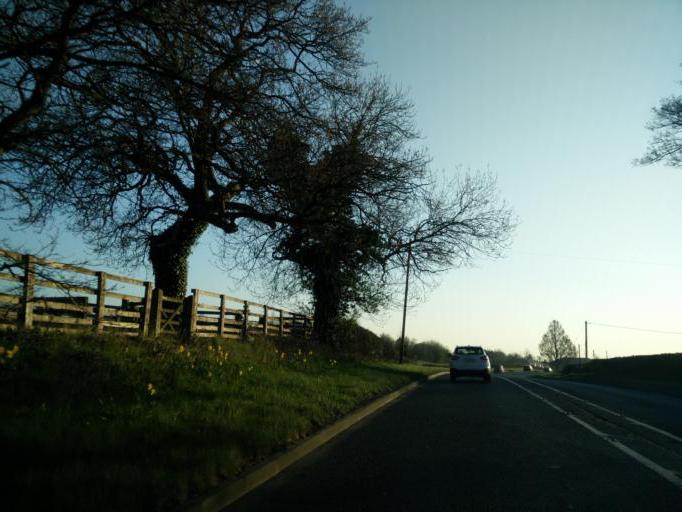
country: GB
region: England
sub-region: County Durham
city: Ushaw Moor
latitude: 54.7461
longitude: -1.6332
